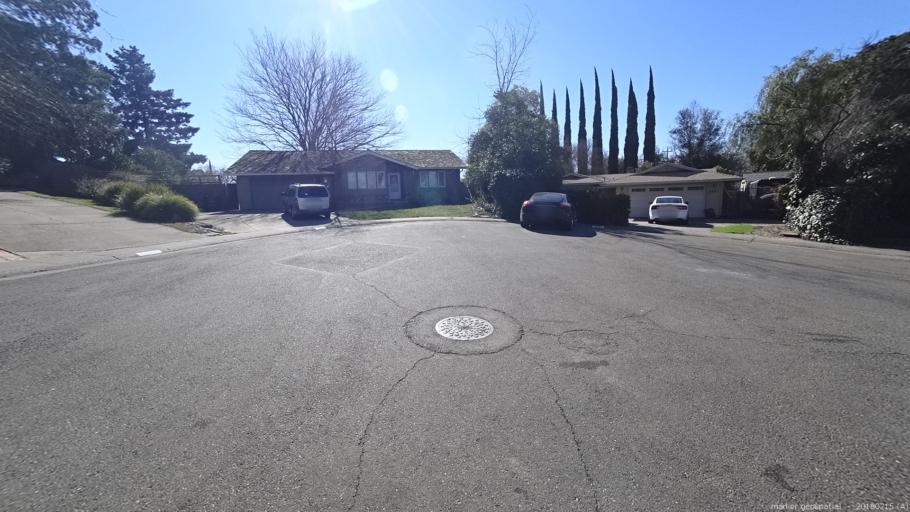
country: US
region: California
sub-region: Sacramento County
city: Foothill Farms
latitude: 38.6733
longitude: -121.3149
